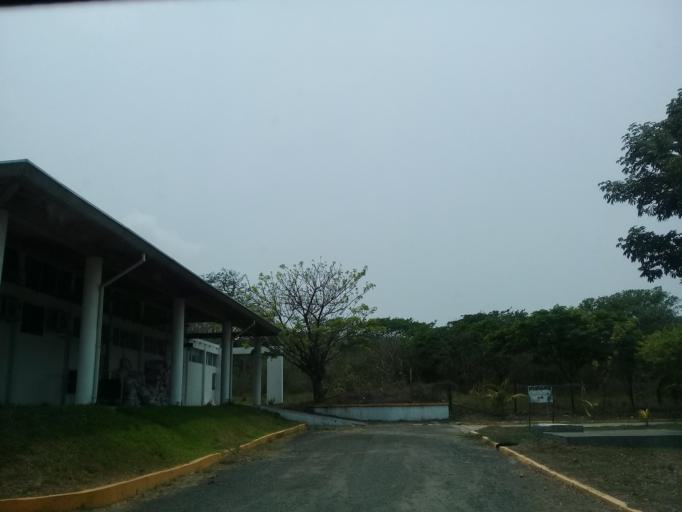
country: MX
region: Veracruz
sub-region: Veracruz
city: Lomas de Rio Medio Cuatro
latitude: 19.1731
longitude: -96.2114
